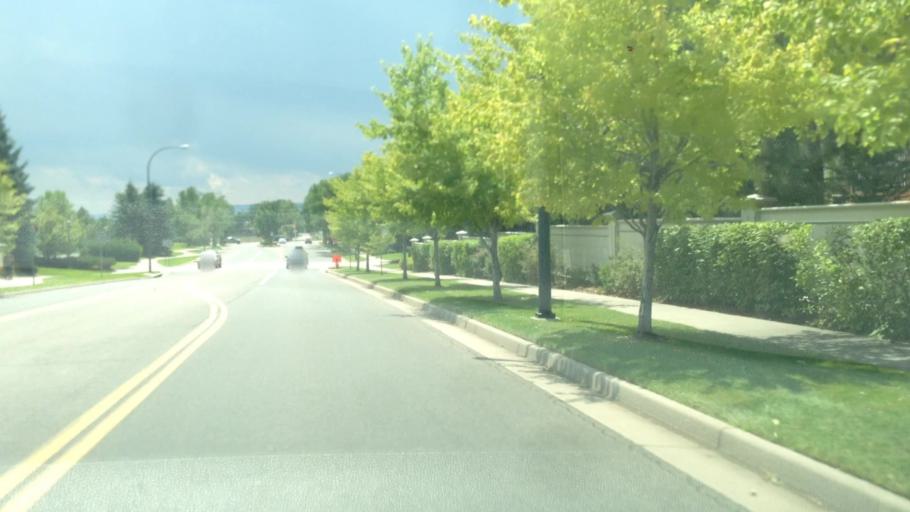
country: US
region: Colorado
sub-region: Arapahoe County
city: Columbine Valley
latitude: 39.6125
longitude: -105.0570
